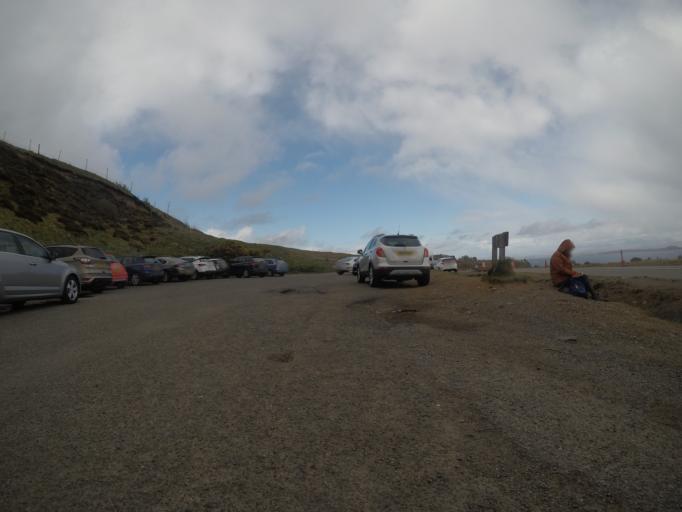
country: GB
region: Scotland
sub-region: Highland
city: Portree
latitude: 57.4975
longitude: -6.1593
